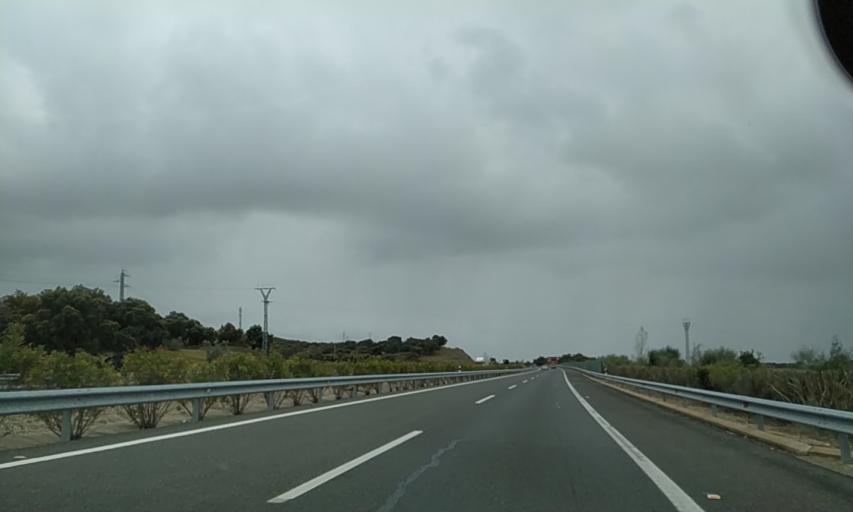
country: ES
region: Extremadura
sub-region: Provincia de Caceres
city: Villar de Plasencia
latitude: 40.1606
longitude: -6.0270
